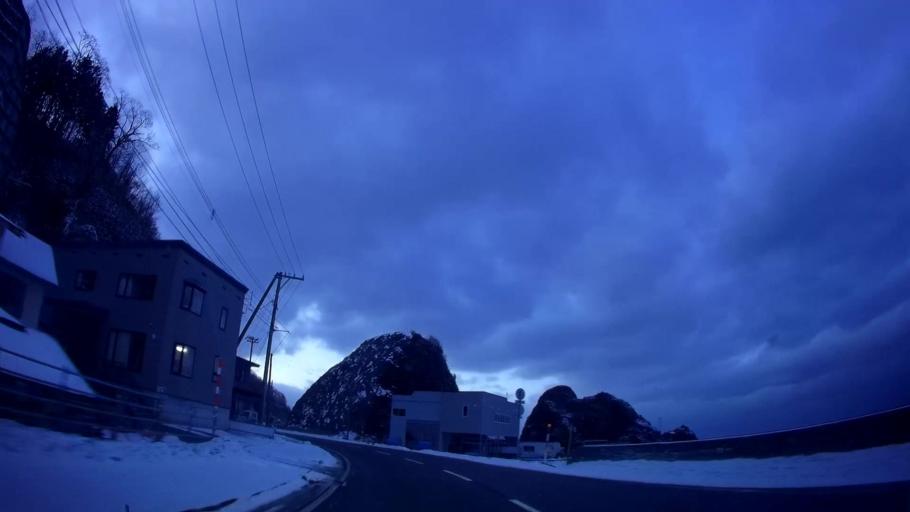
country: JP
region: Hokkaido
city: Hakodate
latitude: 41.8910
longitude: 141.0545
